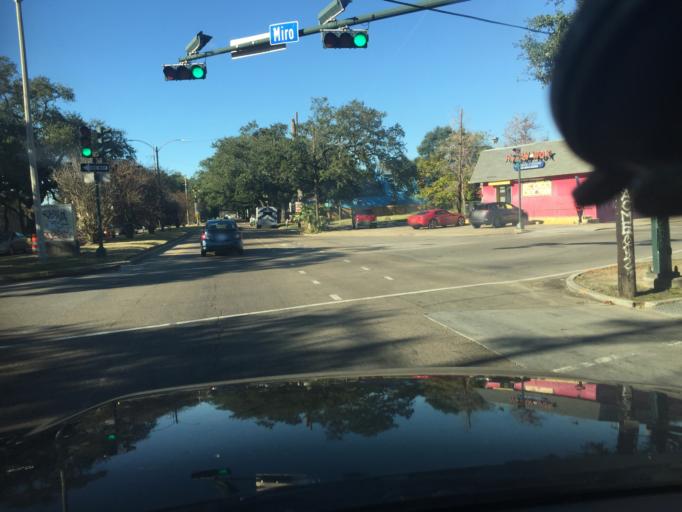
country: US
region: Louisiana
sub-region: Orleans Parish
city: New Orleans
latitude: 29.9785
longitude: -90.0689
